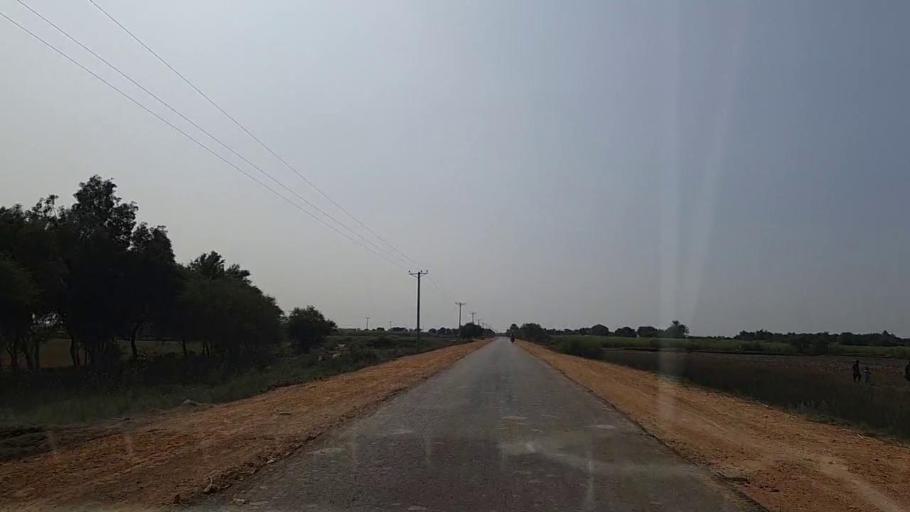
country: PK
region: Sindh
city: Chuhar Jamali
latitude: 24.3562
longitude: 67.9571
